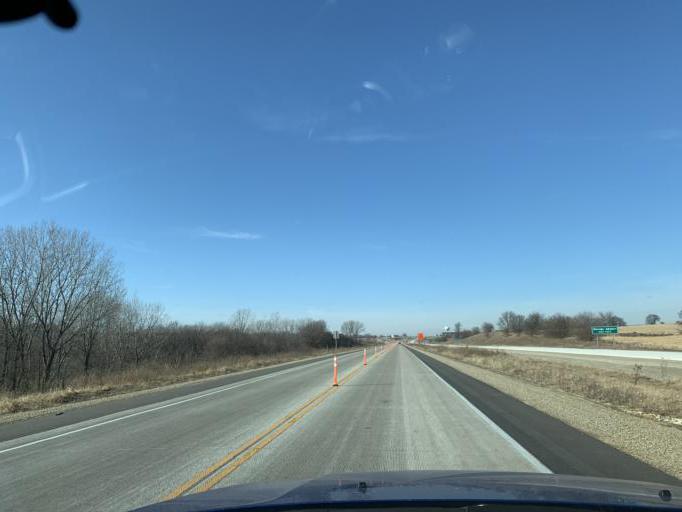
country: US
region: Wisconsin
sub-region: Green County
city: Monroe
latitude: 42.6015
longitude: -89.6054
